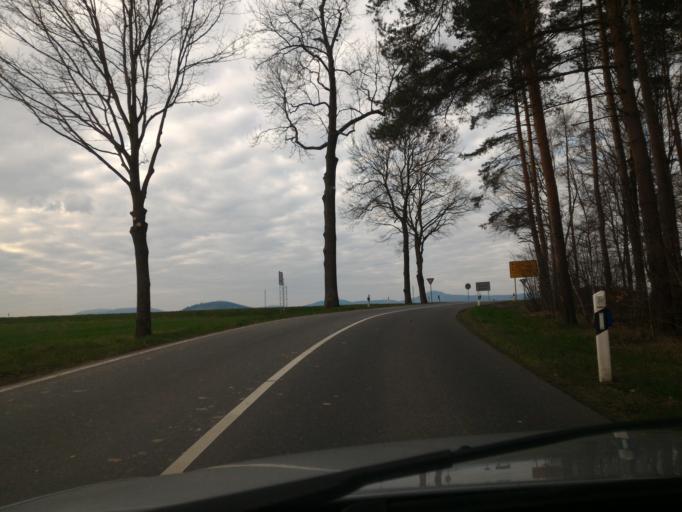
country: DE
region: Saxony
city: Hainewalde
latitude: 50.9315
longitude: 14.7096
